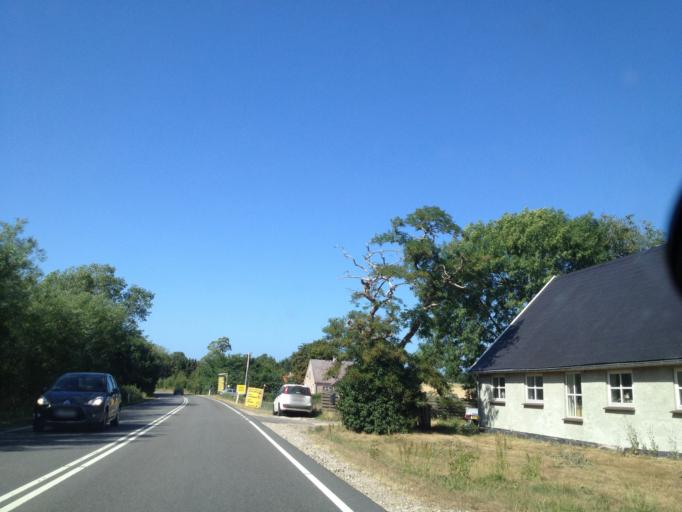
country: DK
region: Capital Region
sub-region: Gribskov Kommune
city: Graested
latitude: 56.0701
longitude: 12.3456
